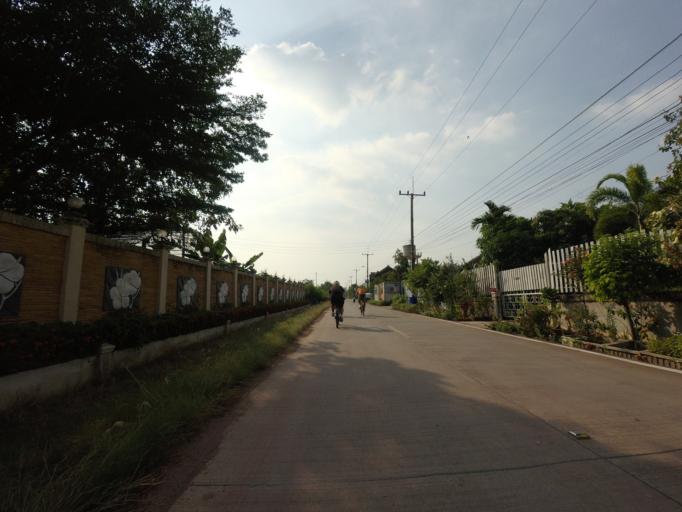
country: TH
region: Samut Sakhon
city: Samut Sakhon
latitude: 13.5079
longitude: 100.3098
